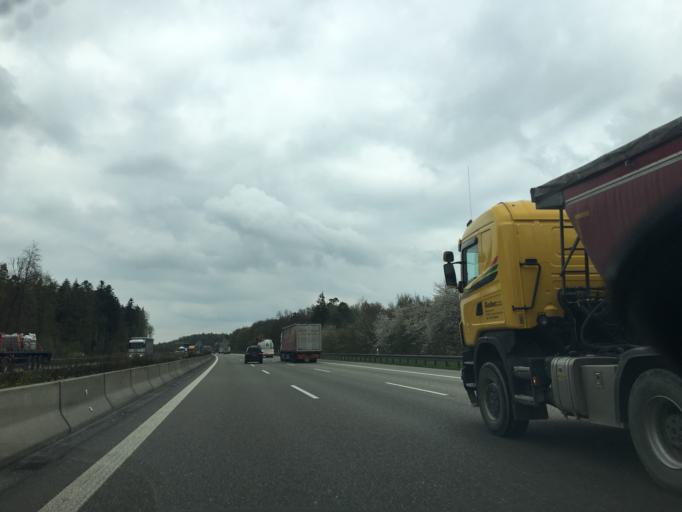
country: DE
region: Baden-Wuerttemberg
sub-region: Karlsruhe Region
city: Niefern-Oschelbronn
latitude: 48.8878
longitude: 8.7873
